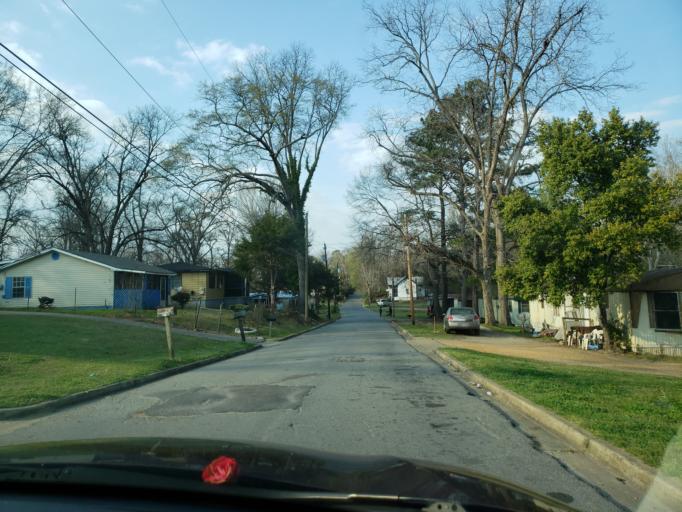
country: US
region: Alabama
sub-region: Hale County
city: Greensboro
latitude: 32.7060
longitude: -87.5991
